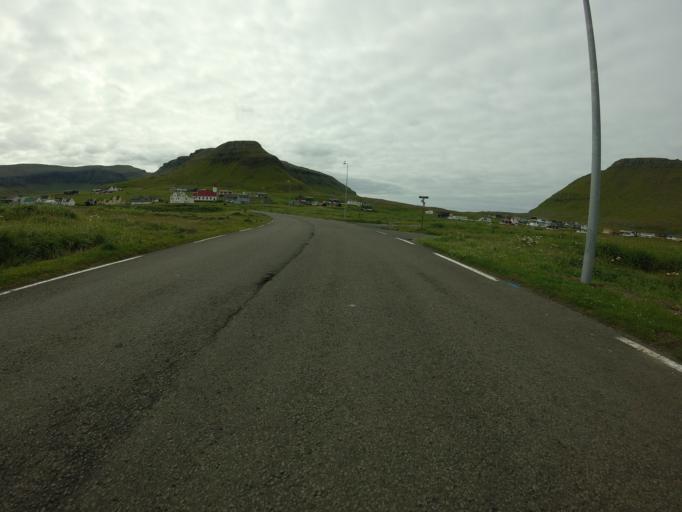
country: FO
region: Suduroy
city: Tvoroyri
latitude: 61.6005
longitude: -6.9533
